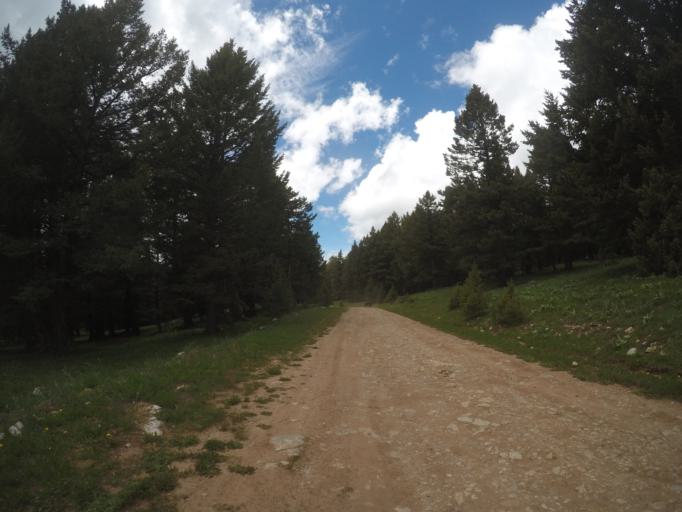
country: US
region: Wyoming
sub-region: Big Horn County
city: Lovell
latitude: 45.1627
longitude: -108.4036
